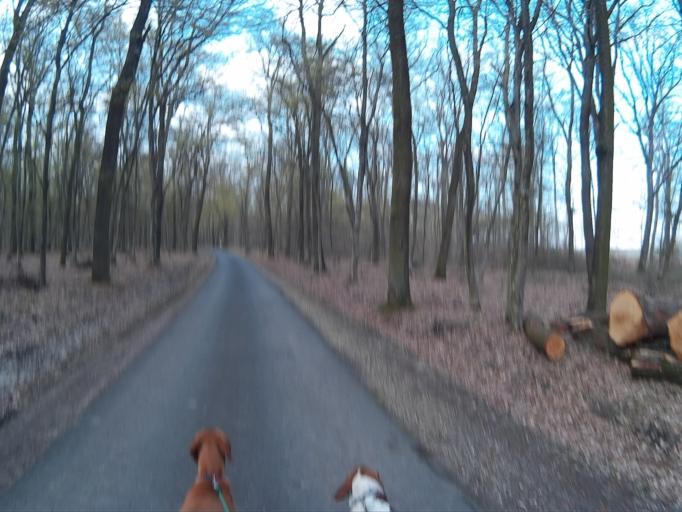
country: HU
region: Vas
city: Sarvar
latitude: 47.1957
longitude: 16.9991
